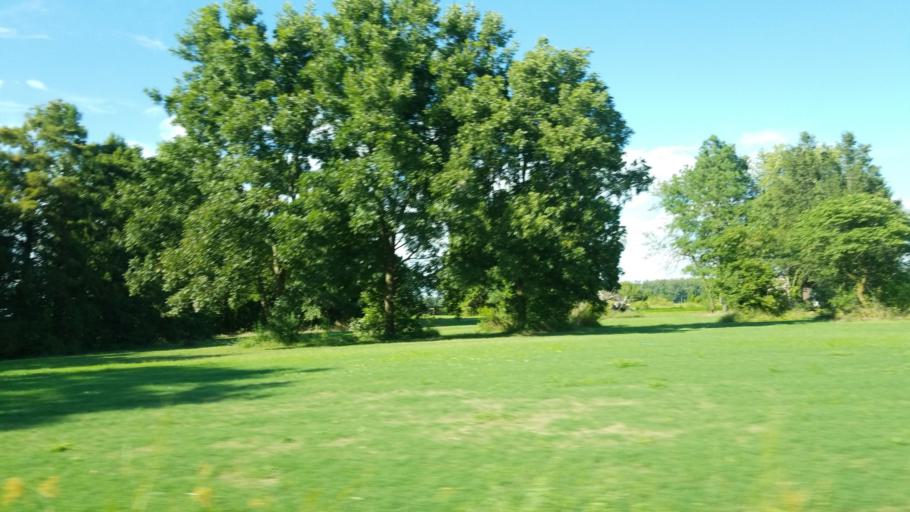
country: US
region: Illinois
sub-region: Saline County
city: Harrisburg
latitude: 37.8164
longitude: -88.5532
